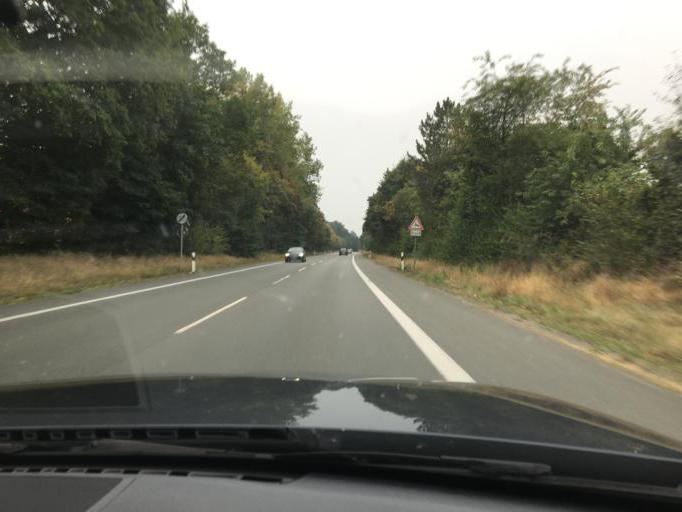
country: DE
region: North Rhine-Westphalia
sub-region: Regierungsbezirk Munster
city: Ladbergen
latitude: 52.1324
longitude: 7.7309
